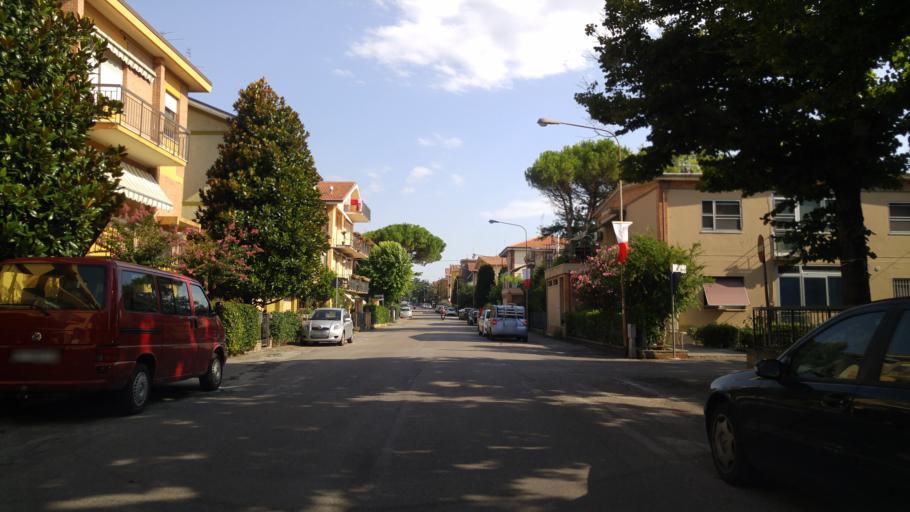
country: IT
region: The Marches
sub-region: Provincia di Pesaro e Urbino
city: Pesaro
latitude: 43.8973
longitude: 12.9231
